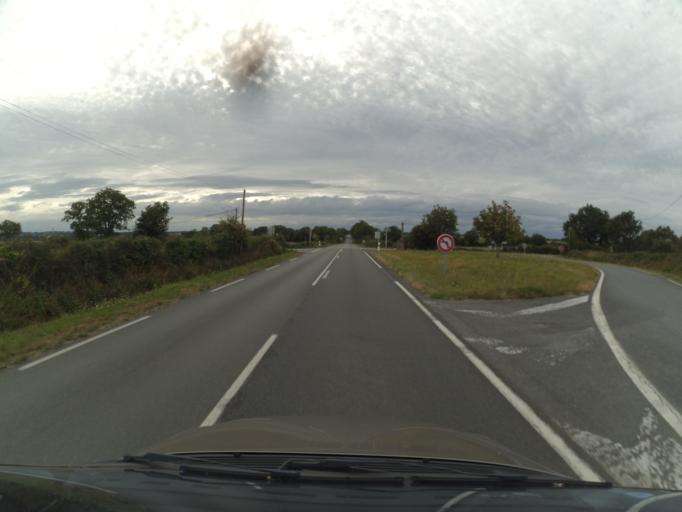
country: FR
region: Pays de la Loire
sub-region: Departement de la Vendee
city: Saint-Aubin-des-Ormeaux
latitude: 47.0146
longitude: -0.9960
